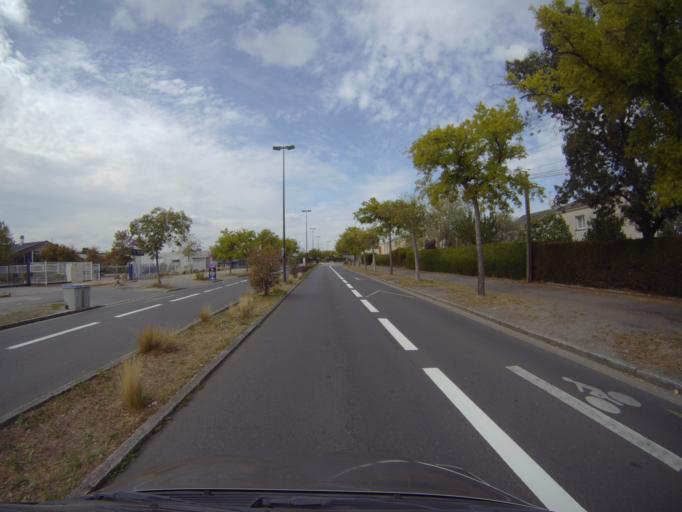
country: FR
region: Pays de la Loire
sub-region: Departement de la Loire-Atlantique
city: Bouguenais
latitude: 47.1992
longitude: -1.6100
